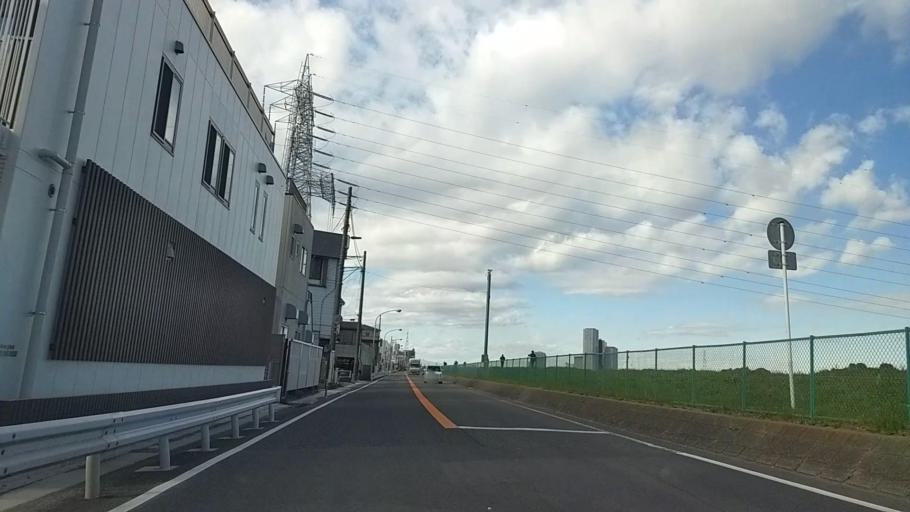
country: JP
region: Kanagawa
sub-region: Kawasaki-shi
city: Kawasaki
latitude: 35.5936
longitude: 139.6459
